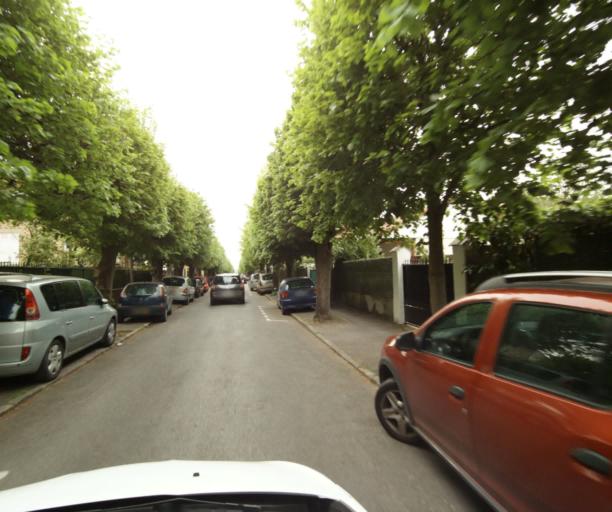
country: FR
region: Ile-de-France
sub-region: Departement de Seine-et-Marne
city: Torcy
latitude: 48.8503
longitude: 2.6466
